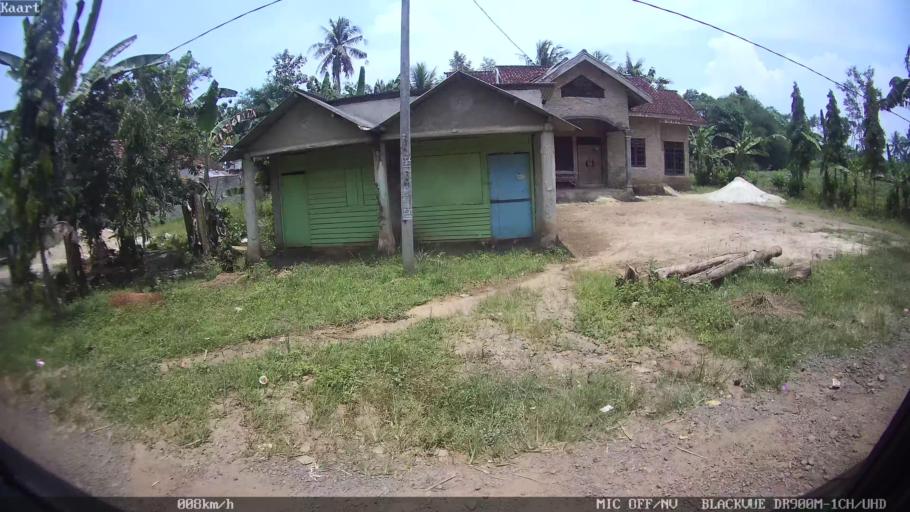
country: ID
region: Lampung
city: Natar
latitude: -5.3158
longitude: 105.2426
